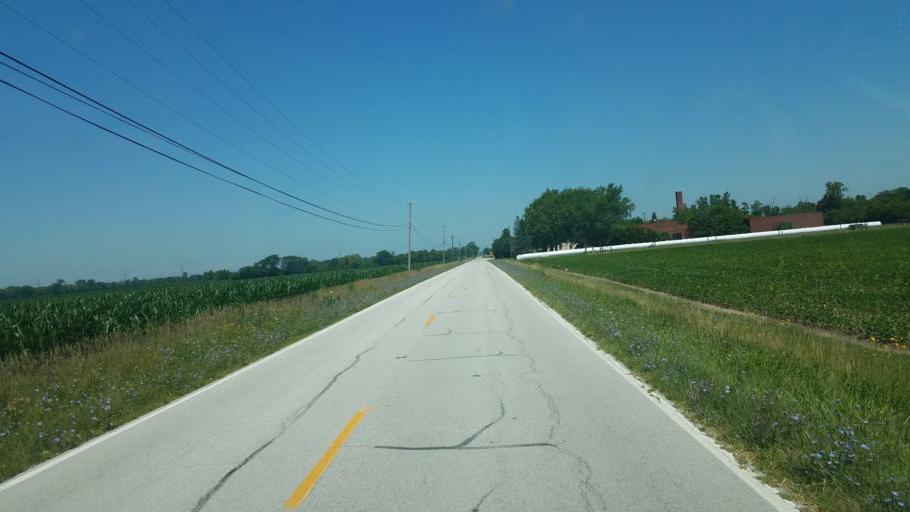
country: US
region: Ohio
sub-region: Sandusky County
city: Clyde
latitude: 41.3932
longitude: -83.0118
